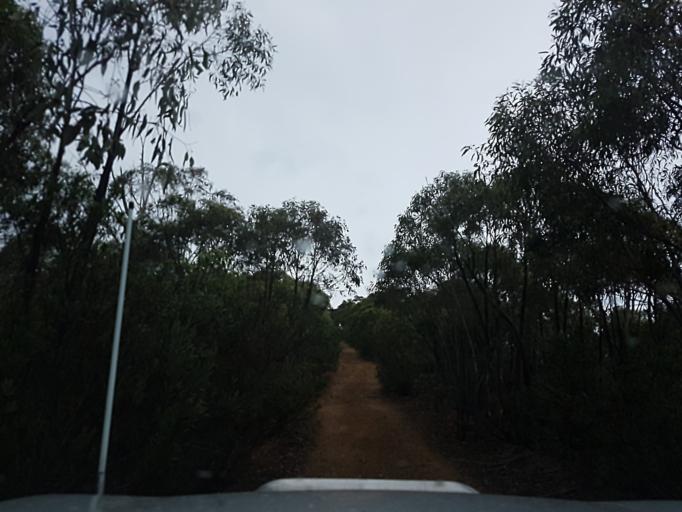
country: AU
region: New South Wales
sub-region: Snowy River
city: Jindabyne
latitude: -36.9190
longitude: 148.3405
